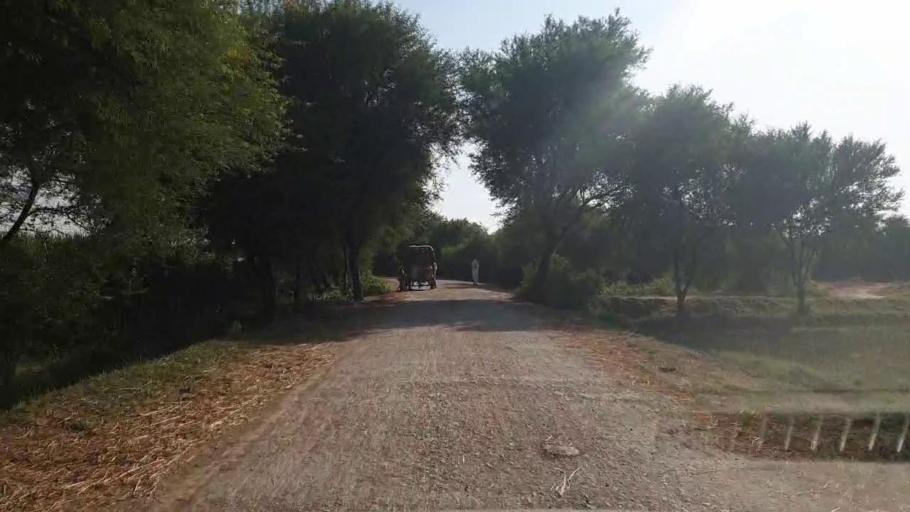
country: PK
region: Sindh
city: Matli
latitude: 25.0164
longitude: 68.7404
